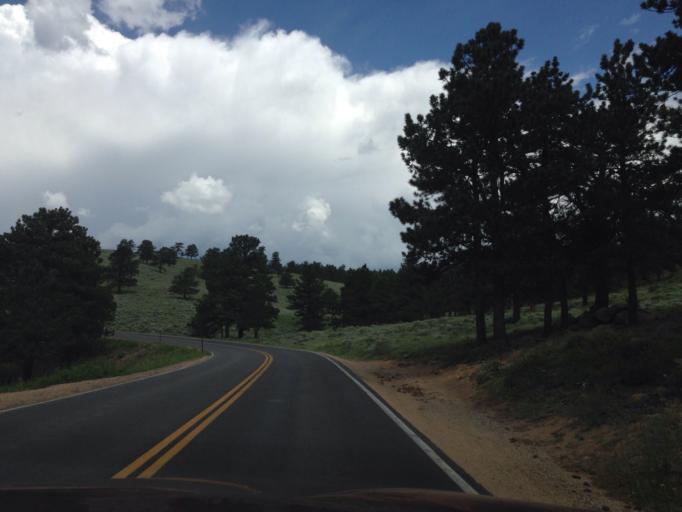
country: US
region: Colorado
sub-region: Larimer County
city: Estes Park
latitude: 40.3811
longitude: -105.6003
